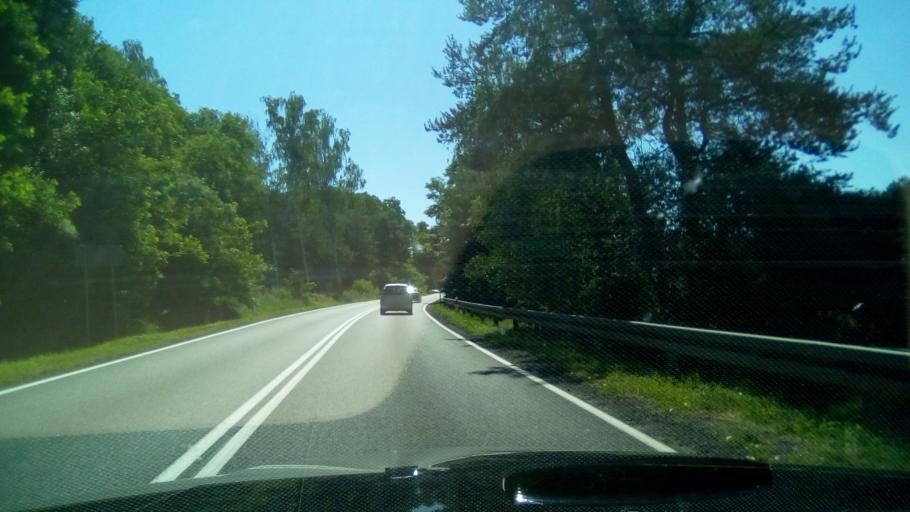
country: PL
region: Lodz Voivodeship
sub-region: Powiat tomaszowski
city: Inowlodz
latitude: 51.5244
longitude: 20.1966
